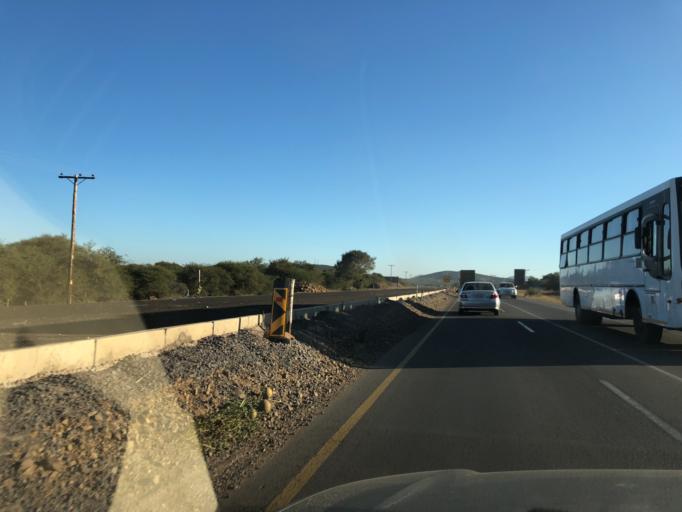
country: BW
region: South East
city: Gaborone
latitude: -24.7239
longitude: 25.8550
